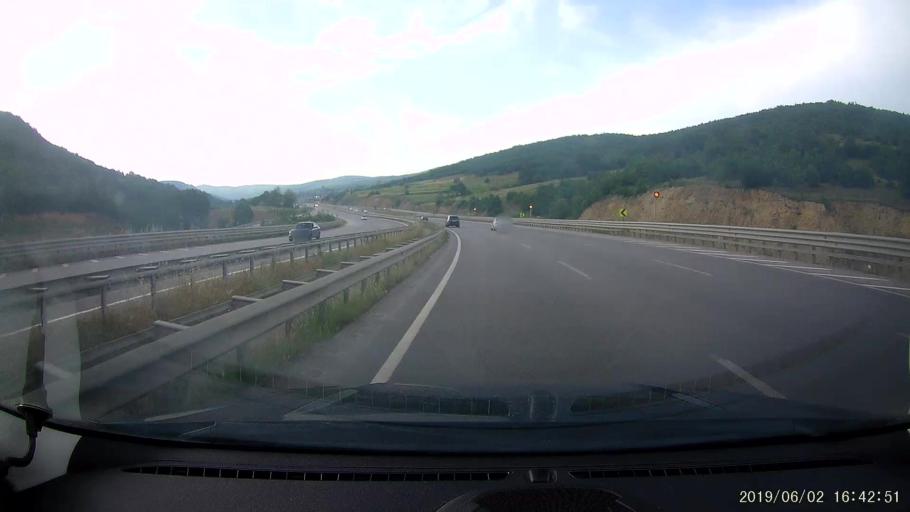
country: TR
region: Samsun
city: Kavak
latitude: 41.1250
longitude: 36.1380
